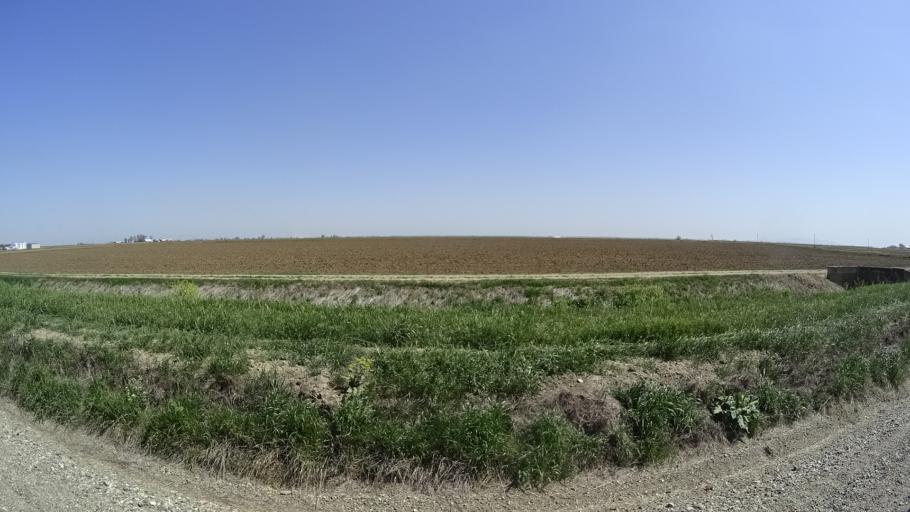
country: US
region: California
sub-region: Glenn County
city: Willows
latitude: 39.4823
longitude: -122.1366
